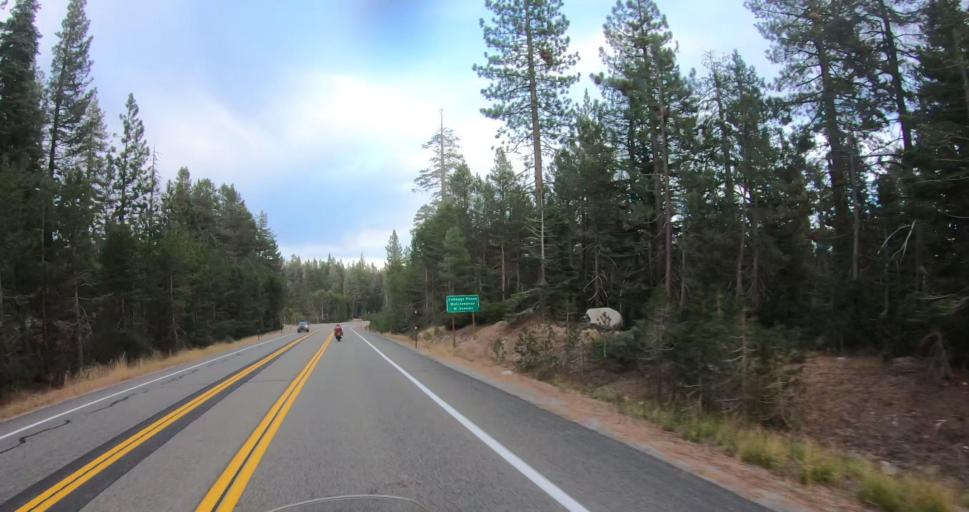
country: US
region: California
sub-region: Calaveras County
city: Arnold
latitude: 38.4141
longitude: -120.1347
